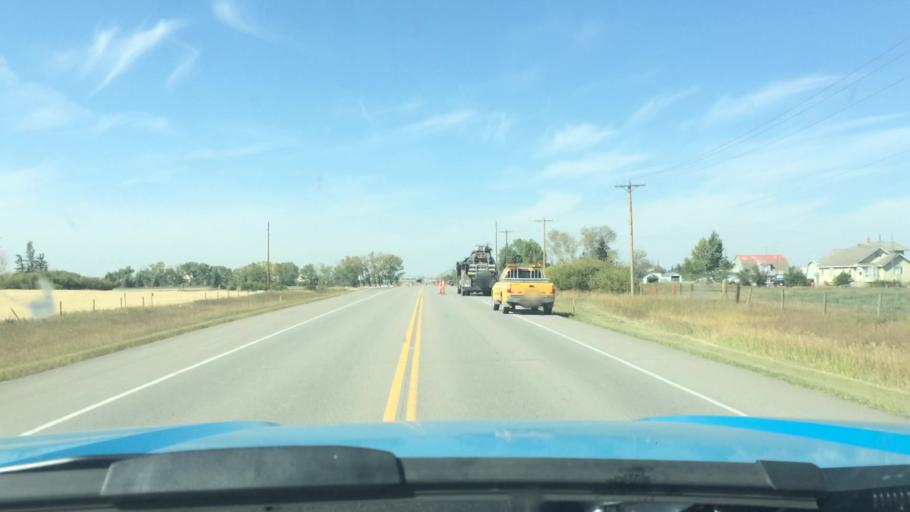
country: CA
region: Alberta
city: Airdrie
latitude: 51.2126
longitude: -113.9544
